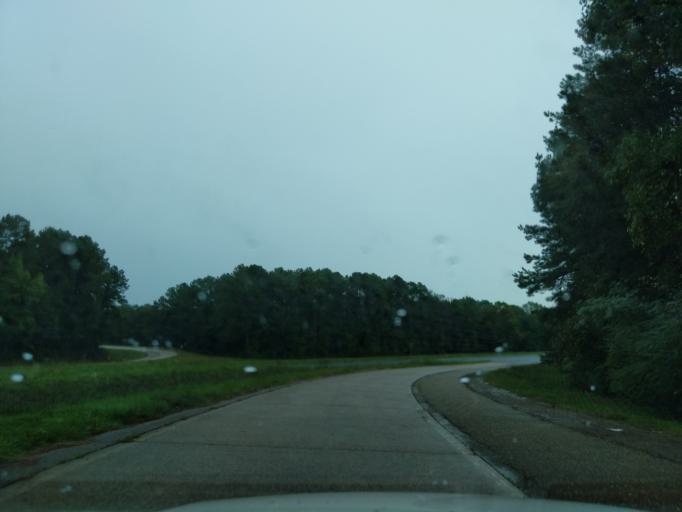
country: US
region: Louisiana
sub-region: Bienville Parish
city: Arcadia
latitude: 32.5627
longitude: -93.0535
